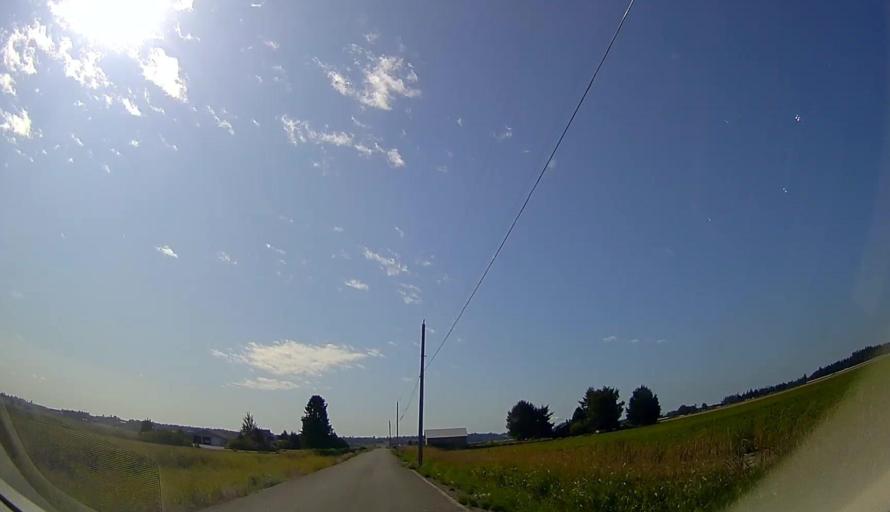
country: US
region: Washington
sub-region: Skagit County
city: Burlington
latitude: 48.4937
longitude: -122.3639
